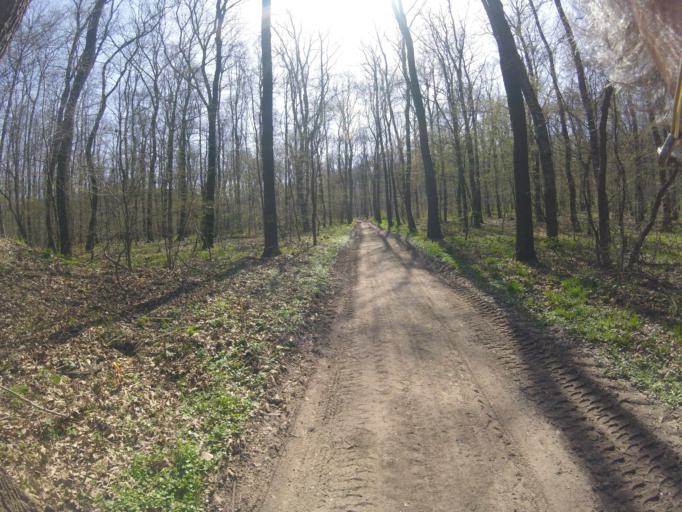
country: HU
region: Pest
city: Pilisszanto
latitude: 47.6526
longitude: 18.8652
